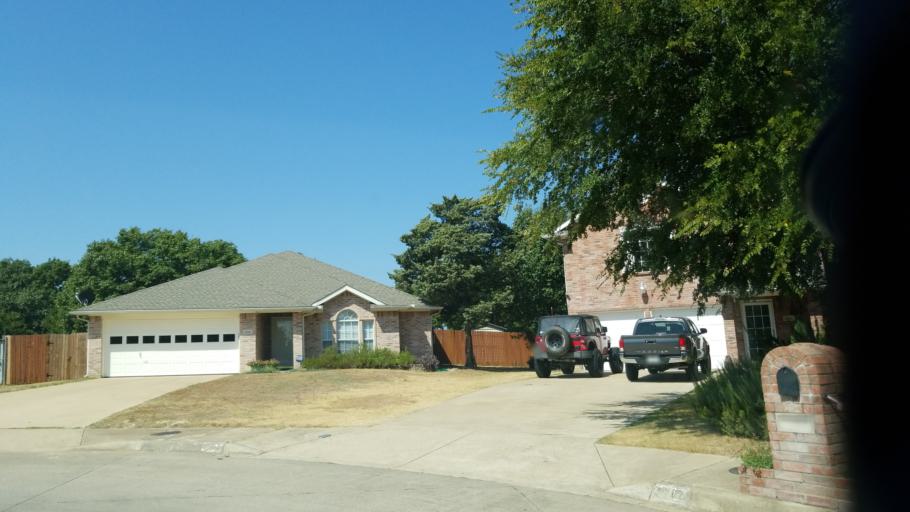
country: US
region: Texas
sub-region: Dallas County
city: Cockrell Hill
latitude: 32.7346
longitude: -96.9167
